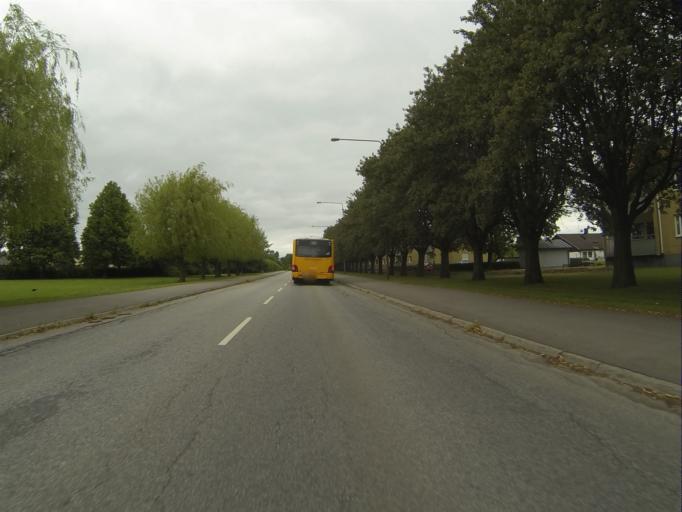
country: SE
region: Skane
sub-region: Staffanstorps Kommun
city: Staffanstorp
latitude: 55.6456
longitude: 13.2076
